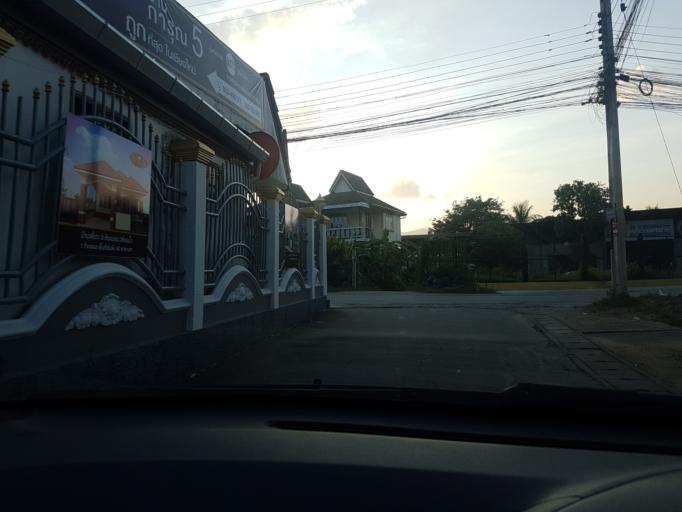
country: TH
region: Chiang Mai
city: San Sai
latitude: 18.8362
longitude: 99.0460
